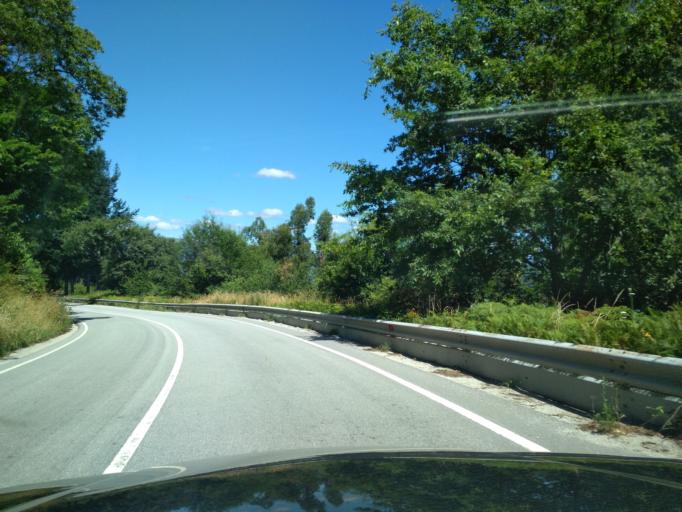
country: PT
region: Vila Real
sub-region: Ribeira de Pena
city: Ribeira de Pena
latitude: 41.5101
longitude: -7.7936
